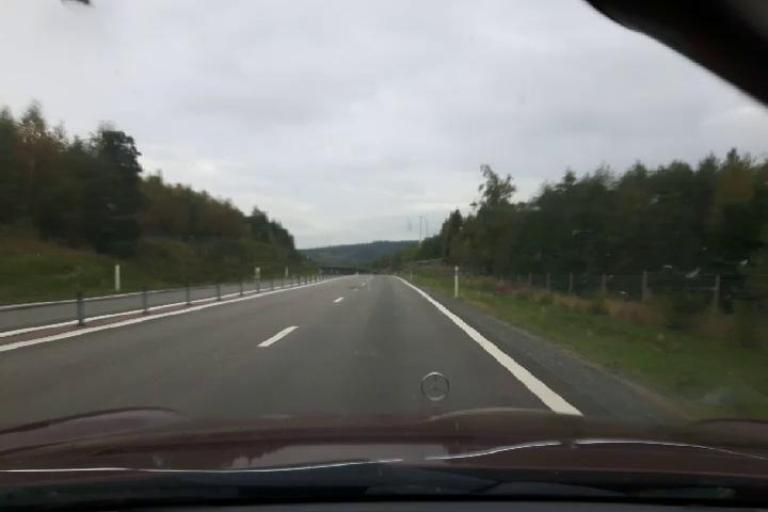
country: SE
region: Vaesternorrland
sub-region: Haernoesands Kommun
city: Haernoesand
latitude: 62.7610
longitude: 17.9051
